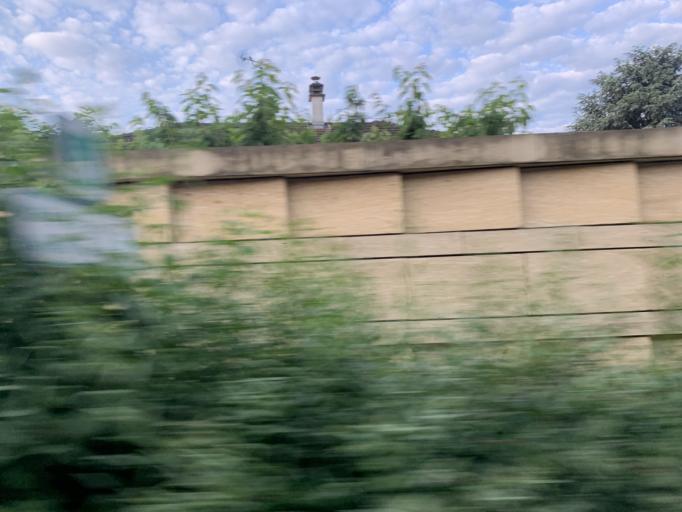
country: FR
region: Rhone-Alpes
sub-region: Departement du Rhone
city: Meyzieu
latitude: 45.7727
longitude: 4.9899
